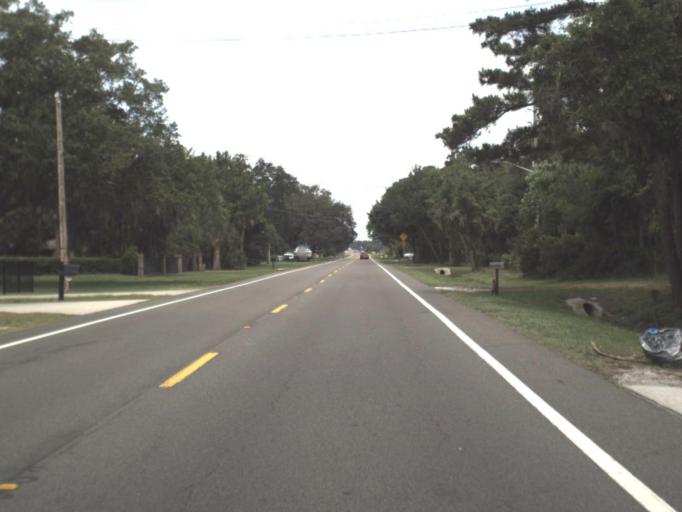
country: US
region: Florida
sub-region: Duval County
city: Atlantic Beach
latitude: 30.4145
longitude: -81.5245
